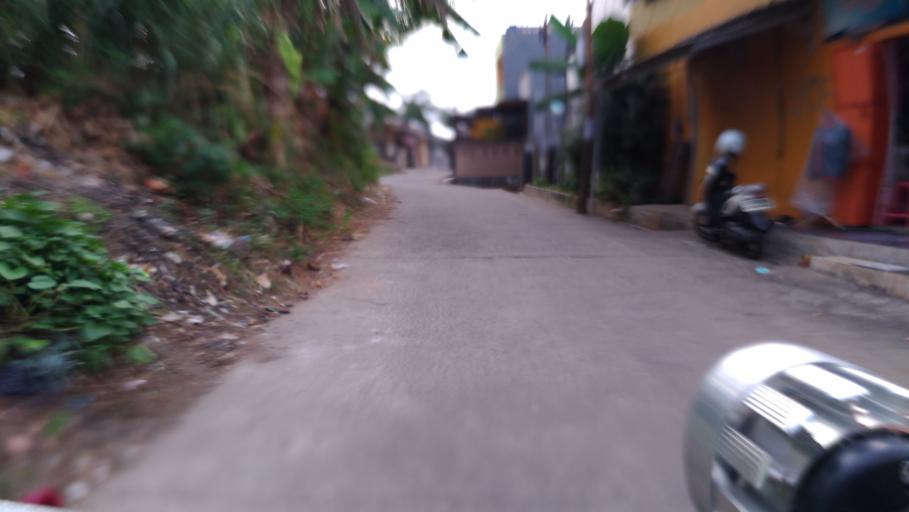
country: ID
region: West Java
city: Depok
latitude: -6.3592
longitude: 106.8683
